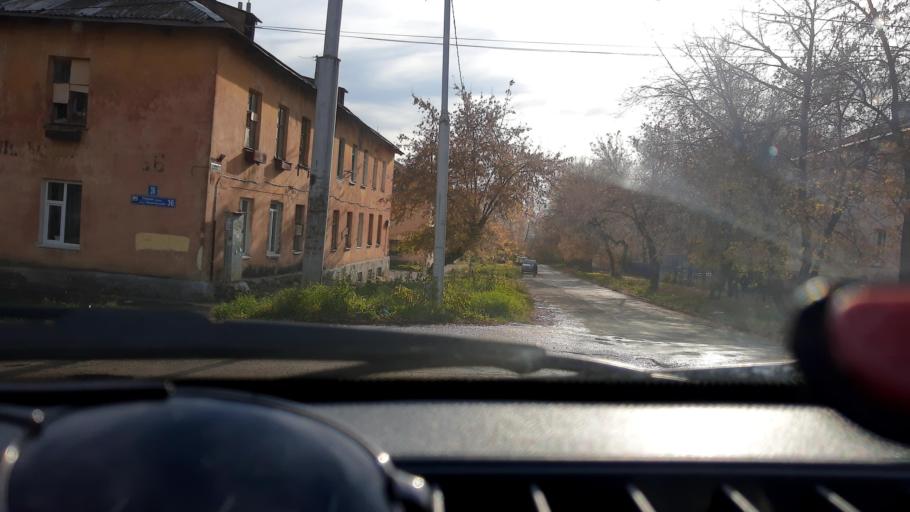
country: RU
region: Bashkortostan
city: Ufa
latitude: 54.8133
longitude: 56.0772
